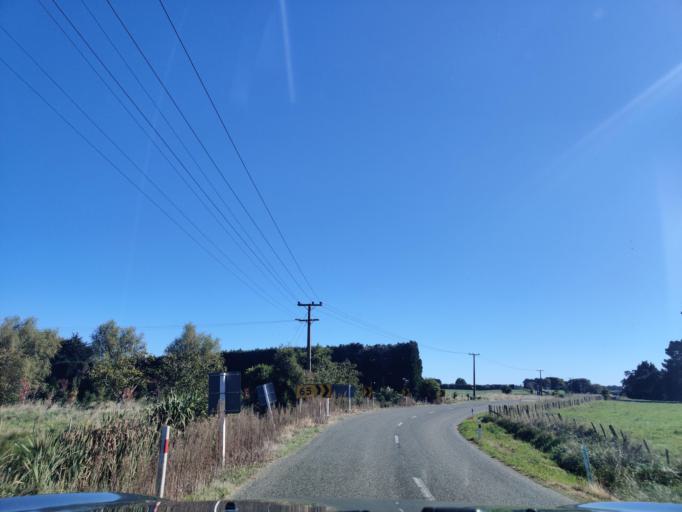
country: NZ
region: Manawatu-Wanganui
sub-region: Palmerston North City
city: Palmerston North
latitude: -40.2371
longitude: 175.6593
